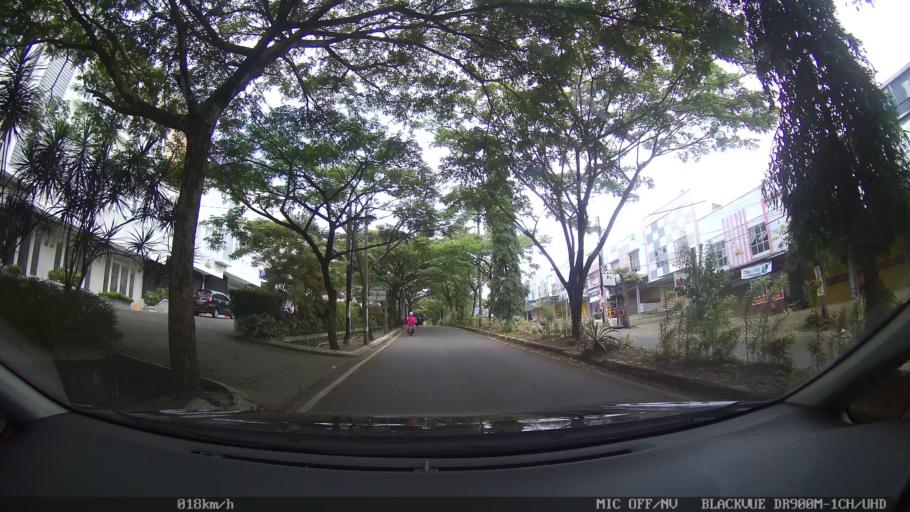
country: ID
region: Lampung
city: Kedaton
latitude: -5.3831
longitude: 105.2110
